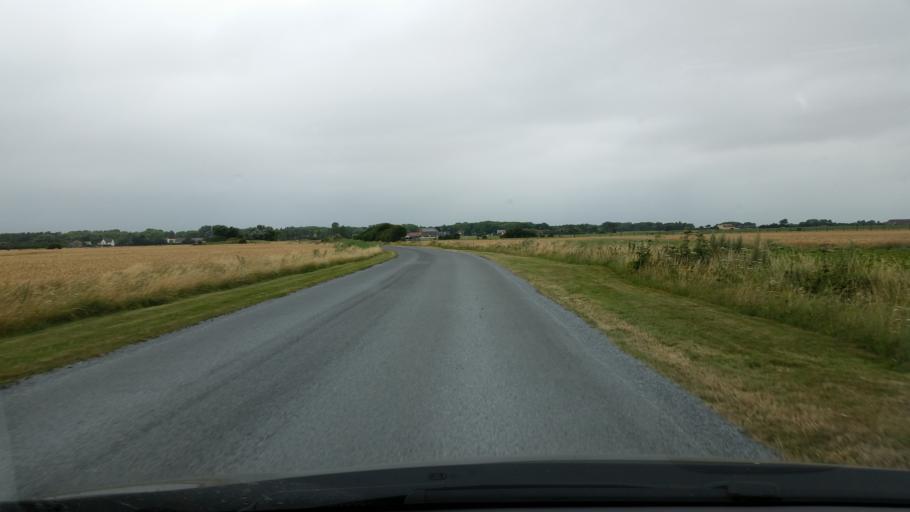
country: FR
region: Nord-Pas-de-Calais
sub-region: Departement du Pas-de-Calais
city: Marck
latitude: 50.9593
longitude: 1.9400
